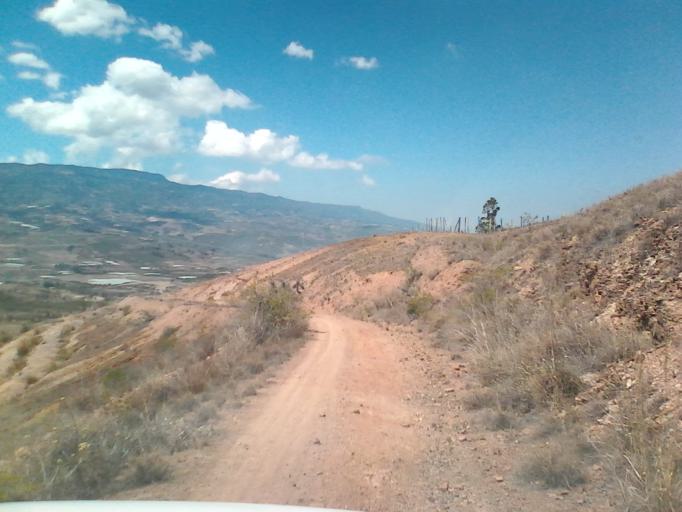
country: CO
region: Boyaca
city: Villa de Leiva
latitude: 5.6107
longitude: -73.5727
